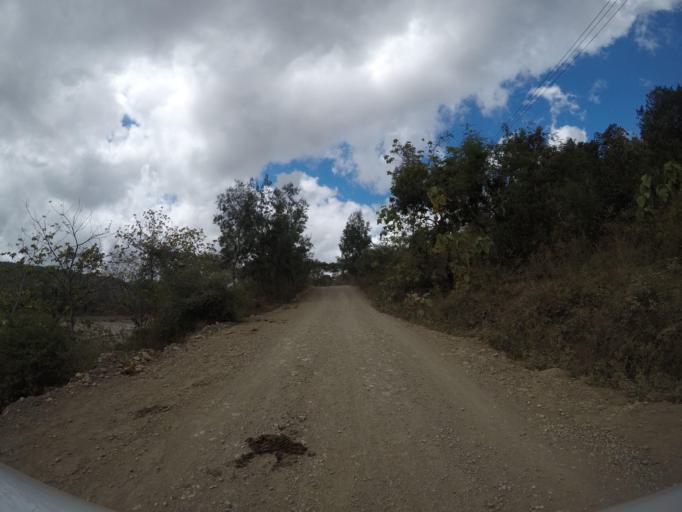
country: TL
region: Lautem
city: Lospalos
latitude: -8.5014
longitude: 126.8294
